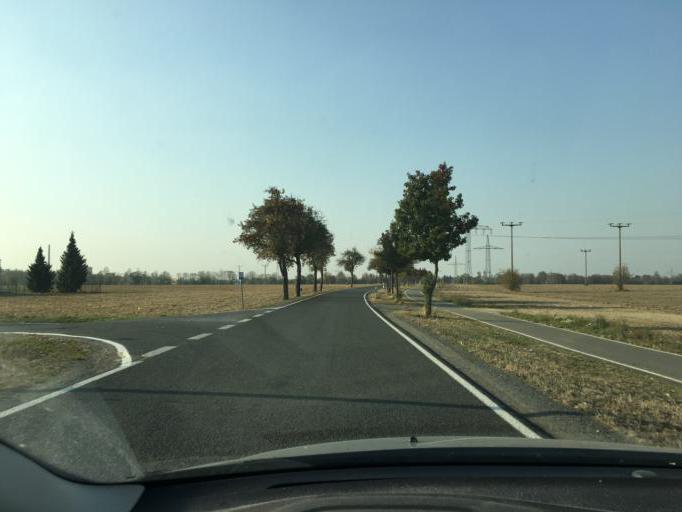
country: DE
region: Saxony
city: Wurzen
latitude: 51.3539
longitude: 12.7519
